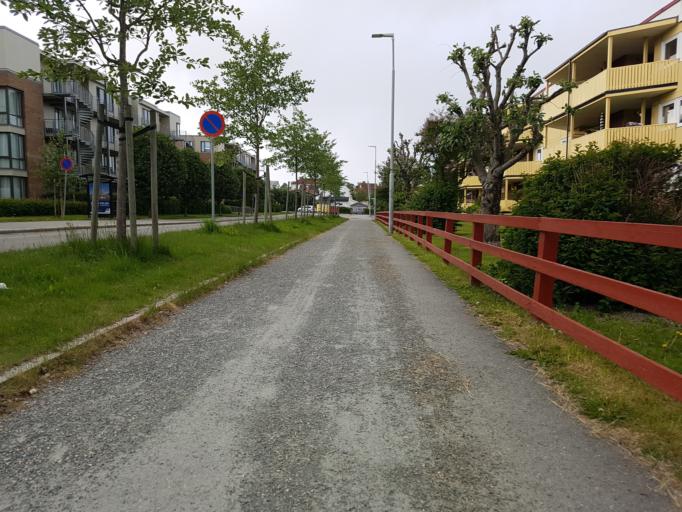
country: NO
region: Sor-Trondelag
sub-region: Trondheim
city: Trondheim
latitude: 63.4323
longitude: 10.4483
